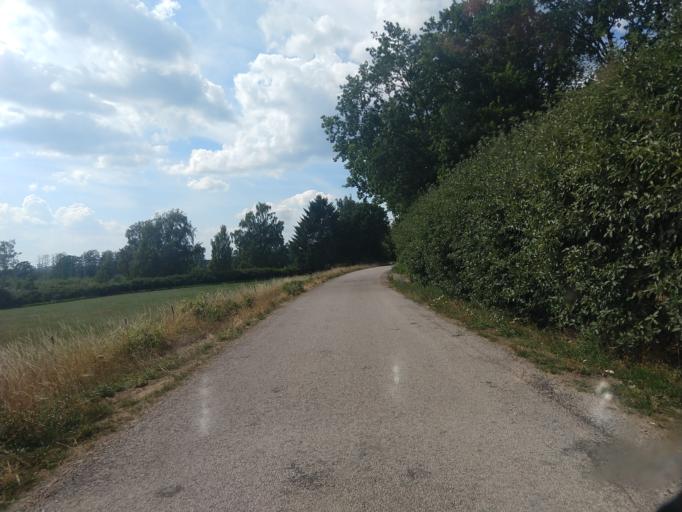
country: SE
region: Blekinge
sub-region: Karlskrona Kommun
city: Nattraby
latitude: 56.2461
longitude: 15.5403
